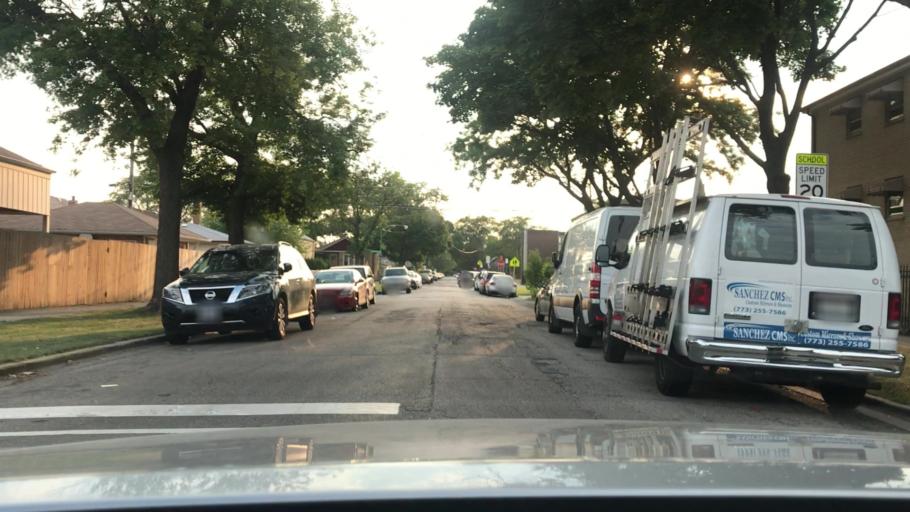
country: US
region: Illinois
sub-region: Cook County
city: Hometown
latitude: 41.7624
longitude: -87.7163
